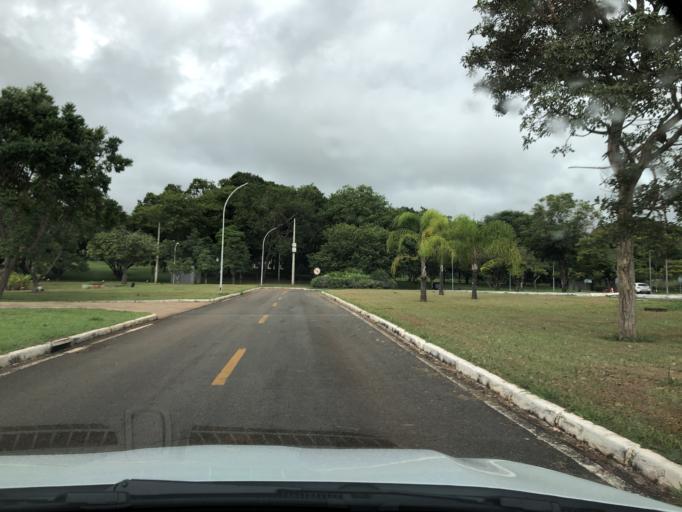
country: BR
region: Federal District
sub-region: Brasilia
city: Brasilia
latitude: -15.7633
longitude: -47.8658
